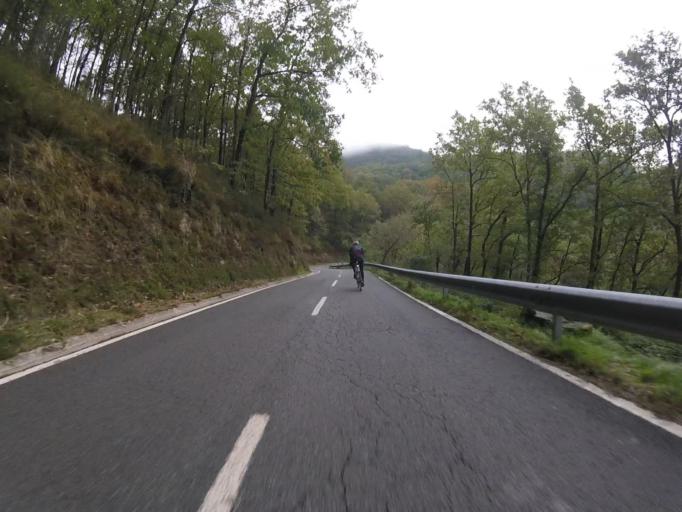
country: ES
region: Navarre
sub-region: Provincia de Navarra
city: Goizueta
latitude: 43.2020
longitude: -1.8588
